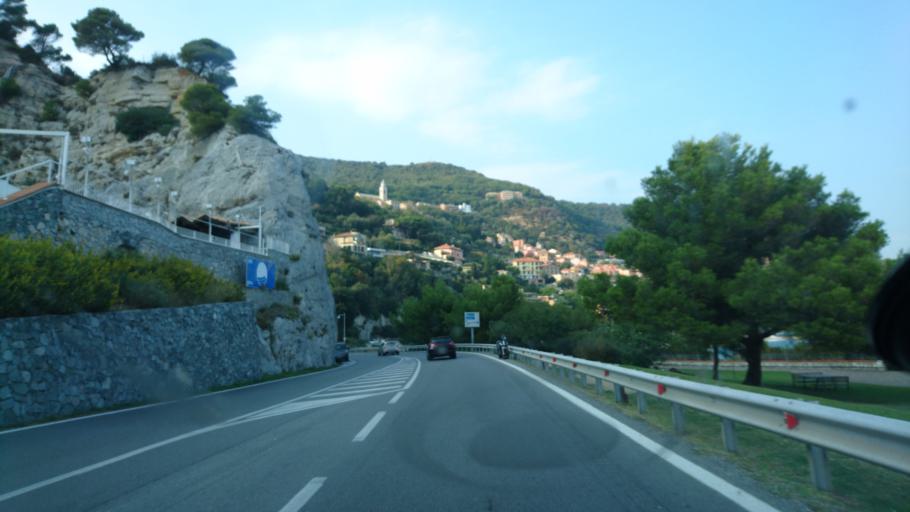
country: IT
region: Liguria
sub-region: Provincia di Savona
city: Bergeggi
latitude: 44.2429
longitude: 8.4447
